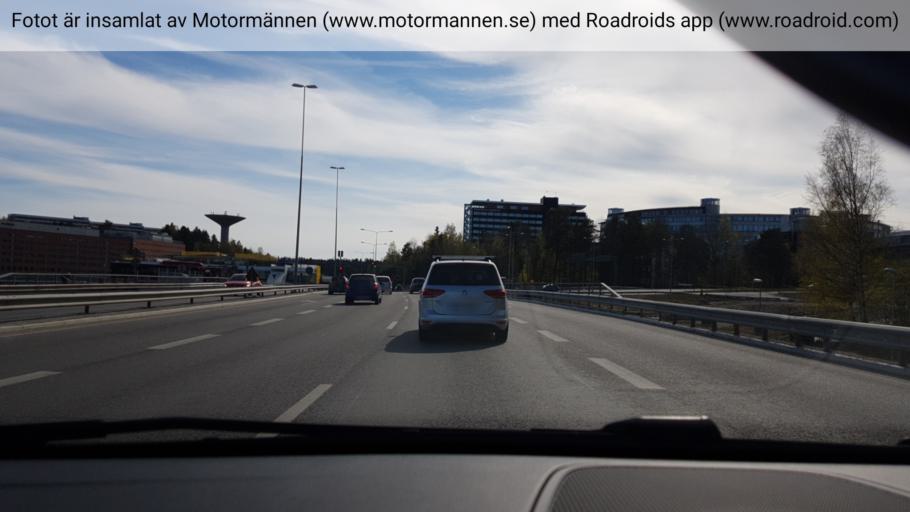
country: SE
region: Stockholm
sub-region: Huddinge Kommun
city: Huddinge
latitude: 59.2207
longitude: 17.9480
